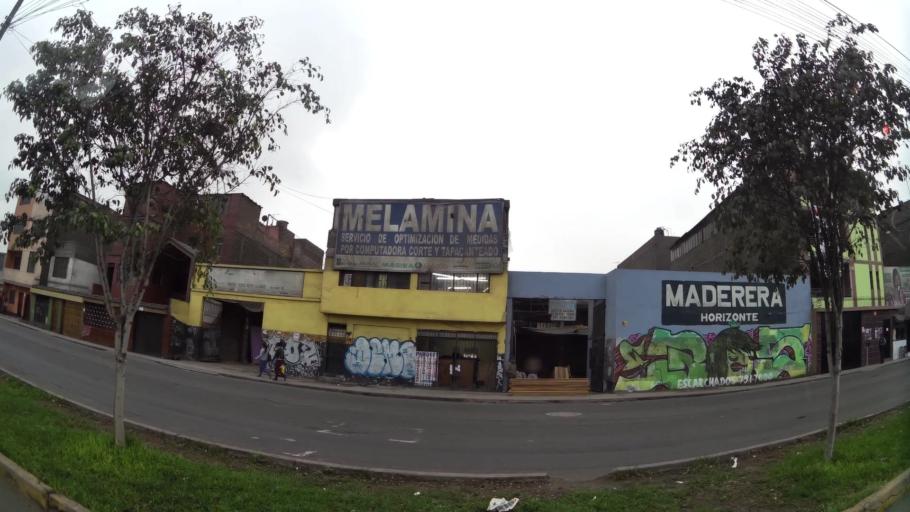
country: PE
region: Lima
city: Lima
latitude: -12.0276
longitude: -77.0005
